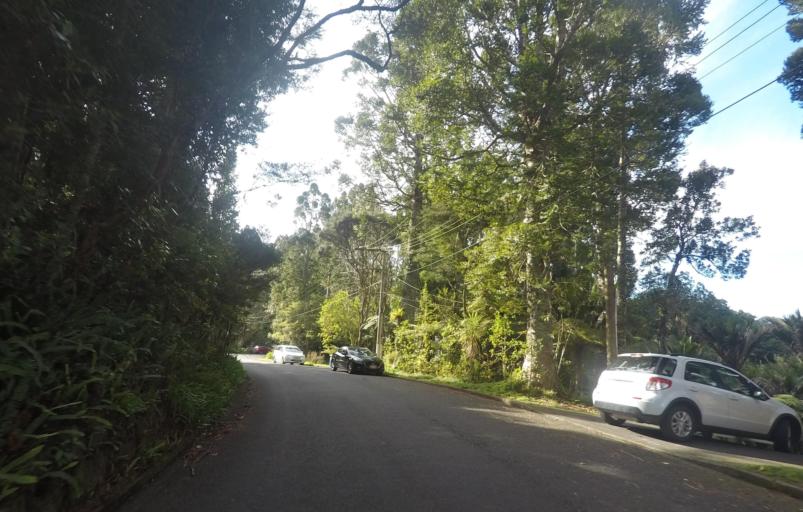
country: NZ
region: Auckland
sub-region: Auckland
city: Titirangi
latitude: -36.9404
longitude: 174.6427
